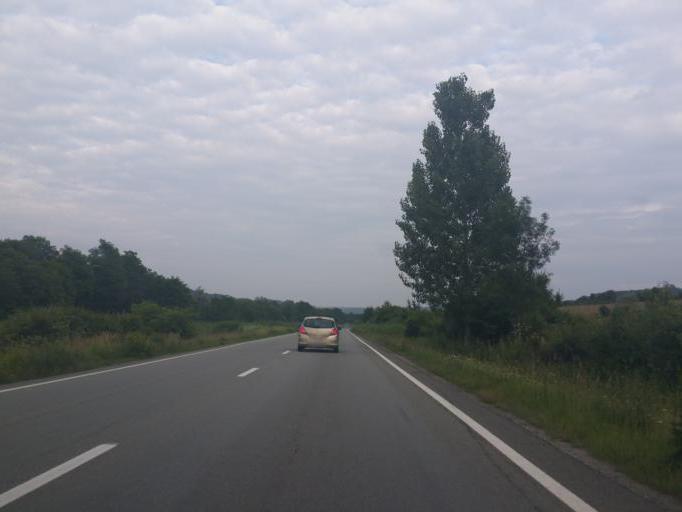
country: RO
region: Salaj
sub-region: Comuna Sanmihaiu Almasului
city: Sanmihaiu Almasului
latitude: 46.9644
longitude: 23.3112
